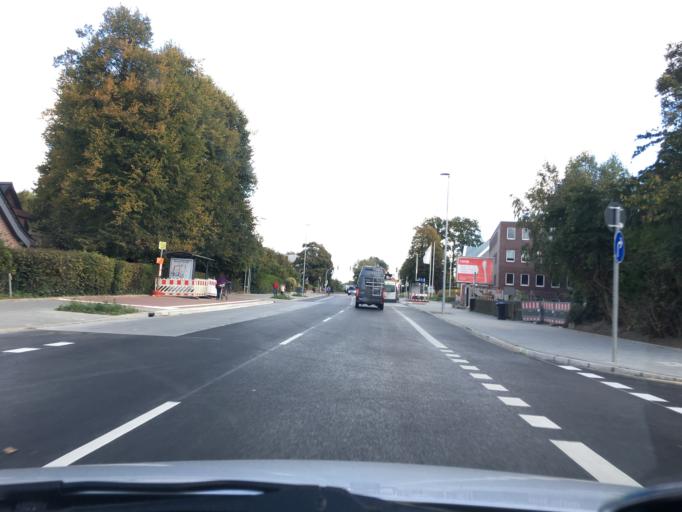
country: DE
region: Schleswig-Holstein
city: Kronshagen
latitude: 54.2994
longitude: 10.0890
